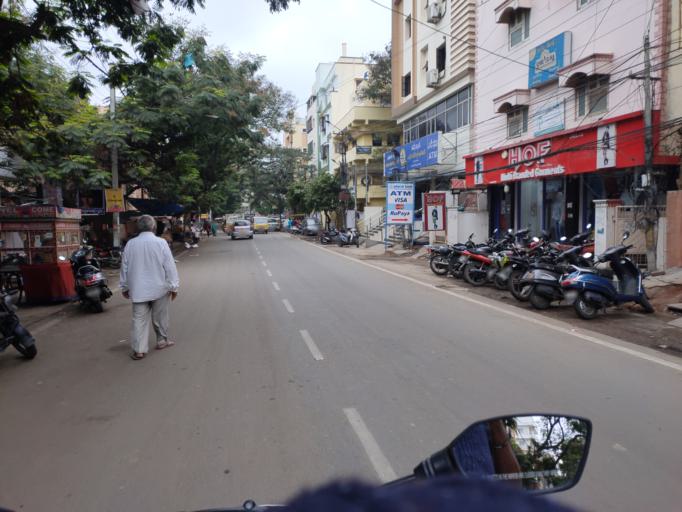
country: IN
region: Telangana
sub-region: Rangareddi
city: Kukatpalli
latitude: 17.4455
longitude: 78.4469
